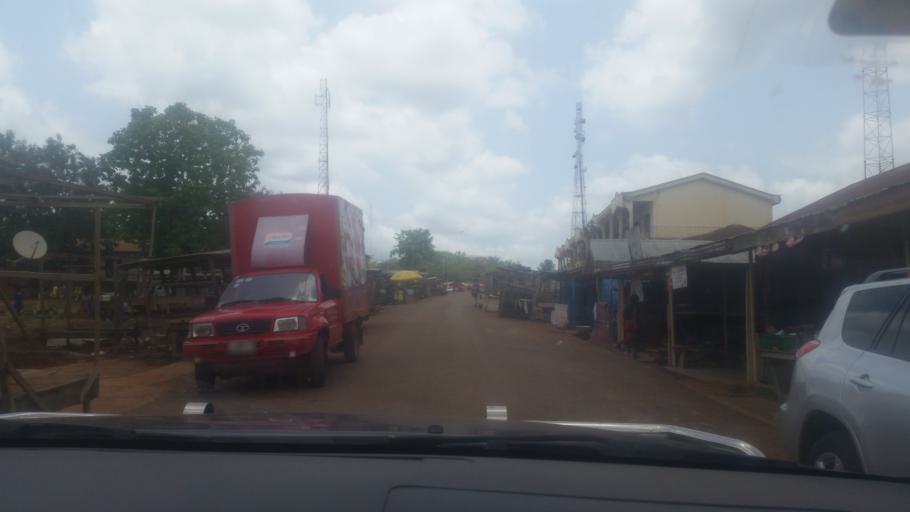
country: GH
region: Western
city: Bibiani
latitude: 6.8048
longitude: -2.5176
